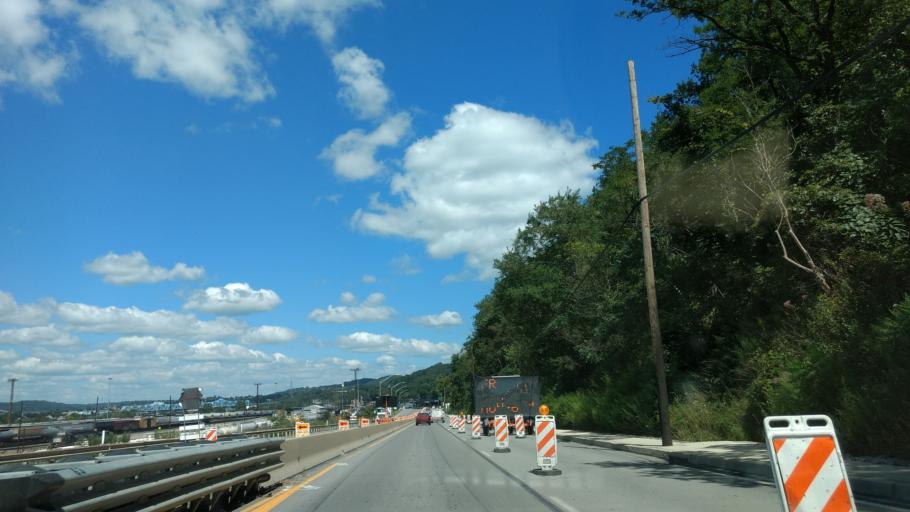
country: US
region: Pennsylvania
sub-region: Beaver County
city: Freedom
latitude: 40.6744
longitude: -80.2467
